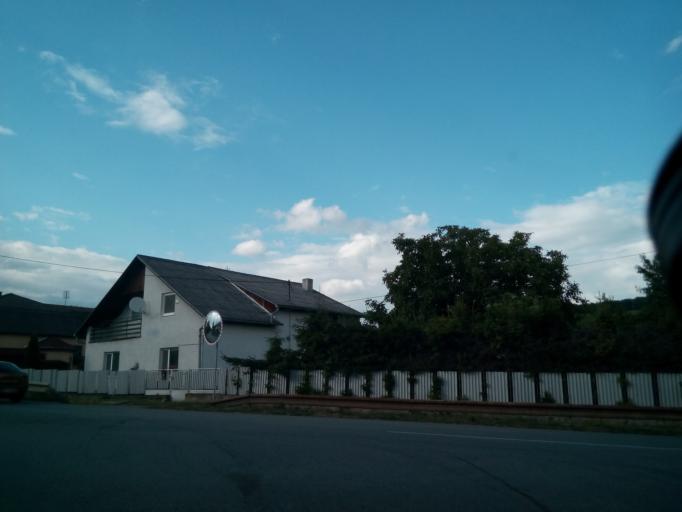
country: SK
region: Kosicky
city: Secovce
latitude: 48.6291
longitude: 21.5241
